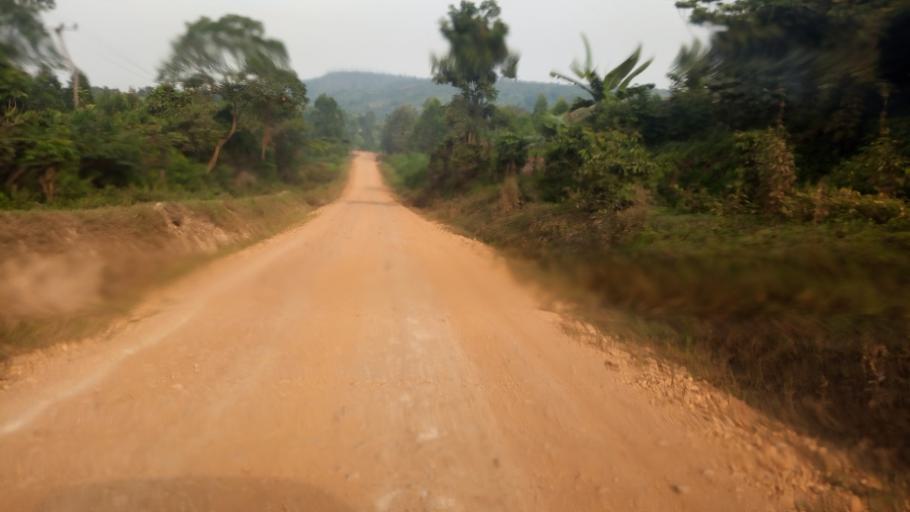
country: UG
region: Western Region
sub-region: Kanungu District
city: Ntungamo
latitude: -0.8388
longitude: 29.6449
